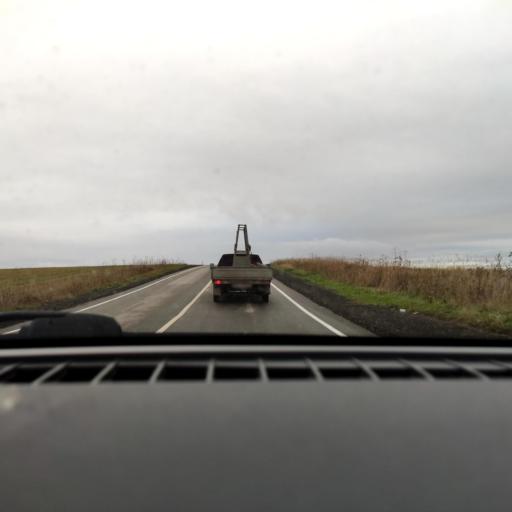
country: RU
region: Perm
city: Ferma
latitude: 57.9210
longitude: 56.3178
